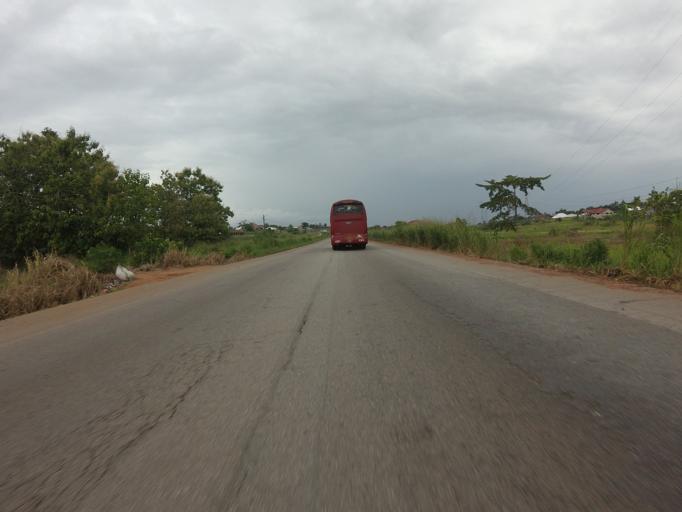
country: GH
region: Ashanti
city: Konongo
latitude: 6.6168
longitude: -1.1739
